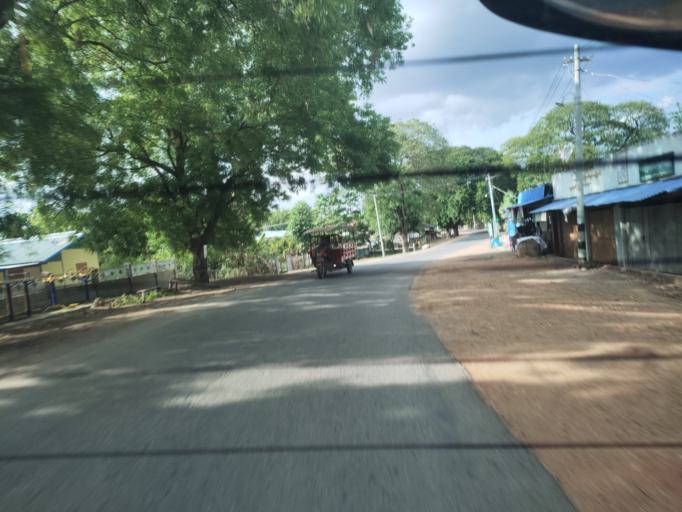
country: MM
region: Magway
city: Magway
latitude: 19.9952
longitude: 94.9889
